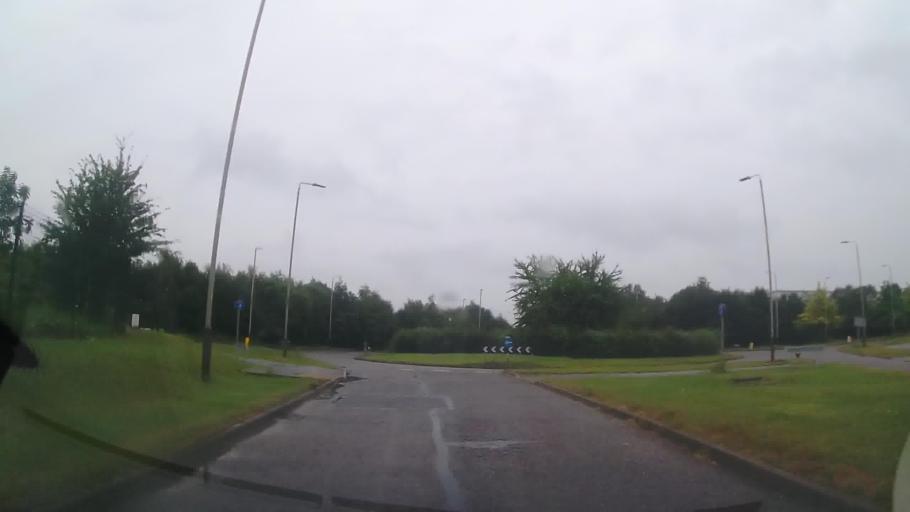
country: GB
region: England
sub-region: Leicestershire
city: Anstey
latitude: 52.6753
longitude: -1.1494
